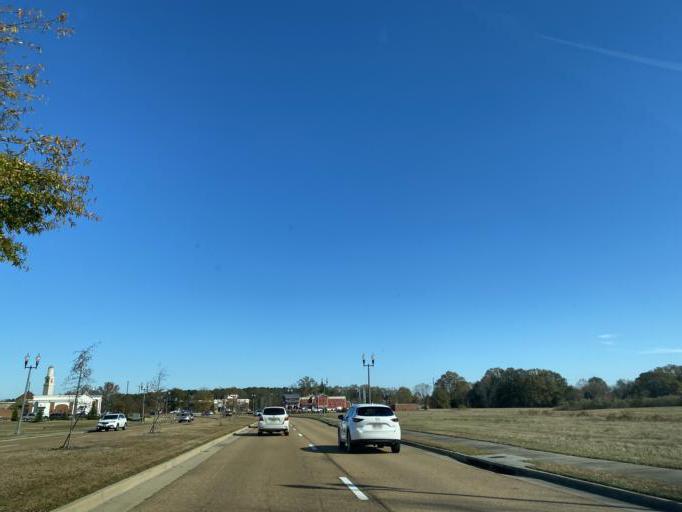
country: US
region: Mississippi
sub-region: Madison County
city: Madison
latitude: 32.4613
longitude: -90.1365
